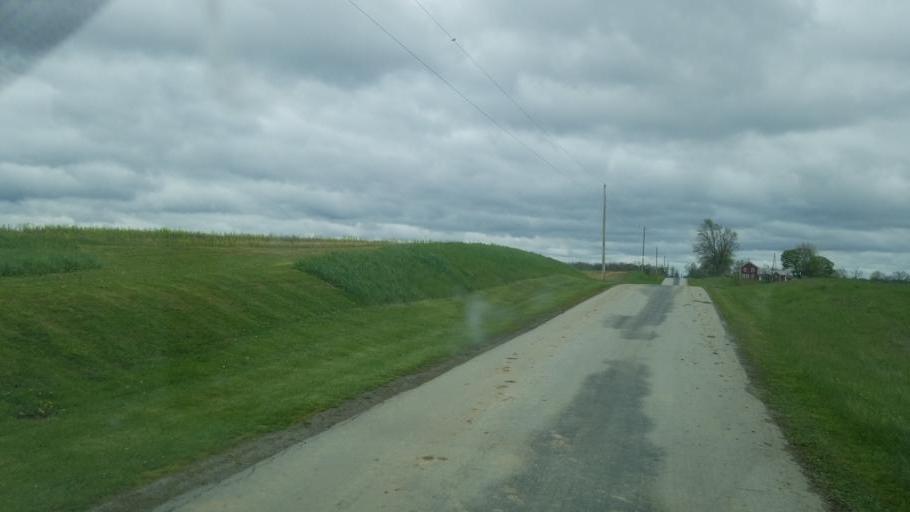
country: US
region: Ohio
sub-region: Wyandot County
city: Upper Sandusky
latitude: 40.7675
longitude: -83.1450
